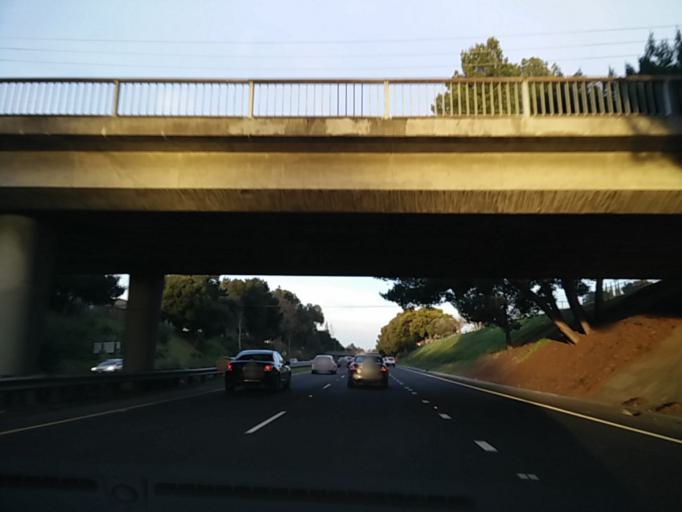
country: US
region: California
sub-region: Santa Clara County
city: Sunnyvale
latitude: 37.3823
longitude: -122.0226
